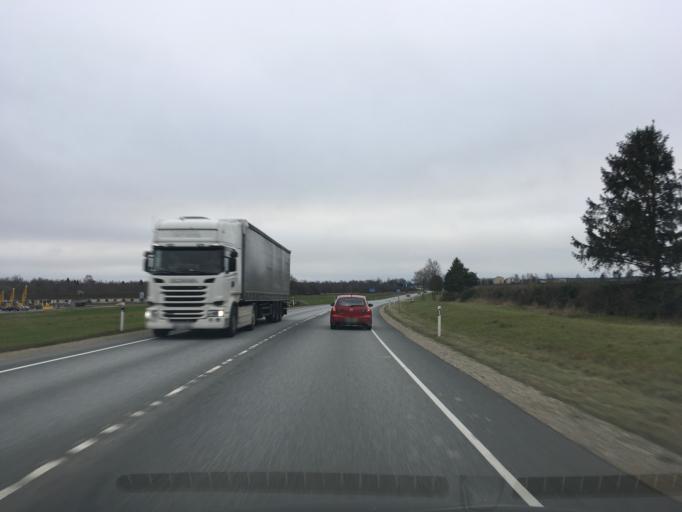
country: EE
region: Laeaene-Virumaa
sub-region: Someru vald
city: Someru
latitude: 59.3725
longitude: 26.4268
